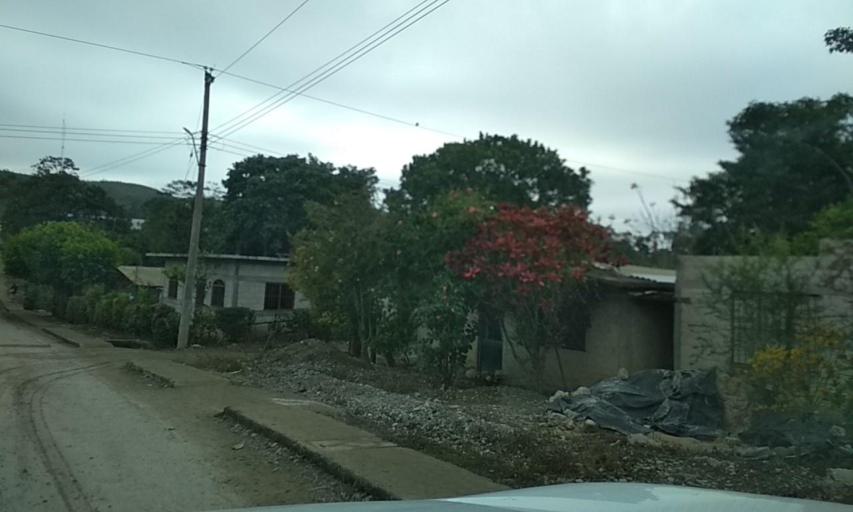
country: MX
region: Veracruz
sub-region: Coatzintla
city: Manuel Maria Contreras
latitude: 20.3602
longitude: -97.5125
